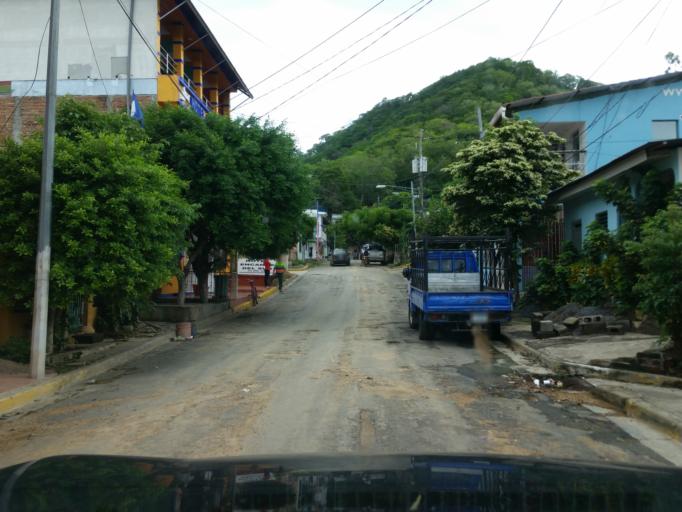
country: NI
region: Rivas
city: San Juan del Sur
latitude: 11.2517
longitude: -85.8702
